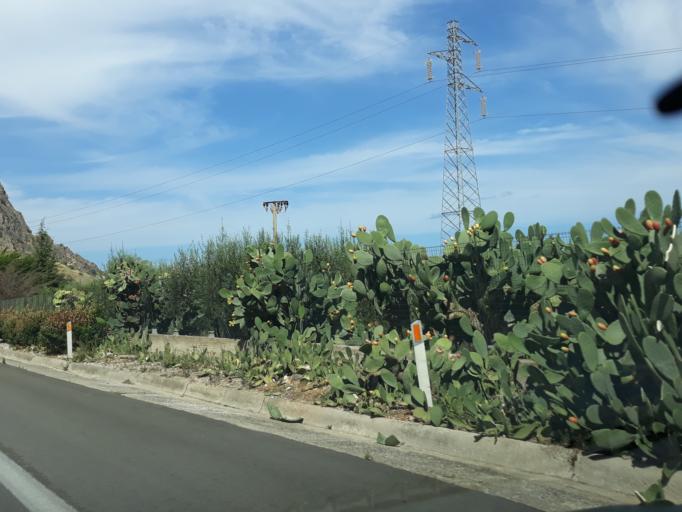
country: IT
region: Sicily
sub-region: Palermo
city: Trabia
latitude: 37.9839
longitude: 13.6597
